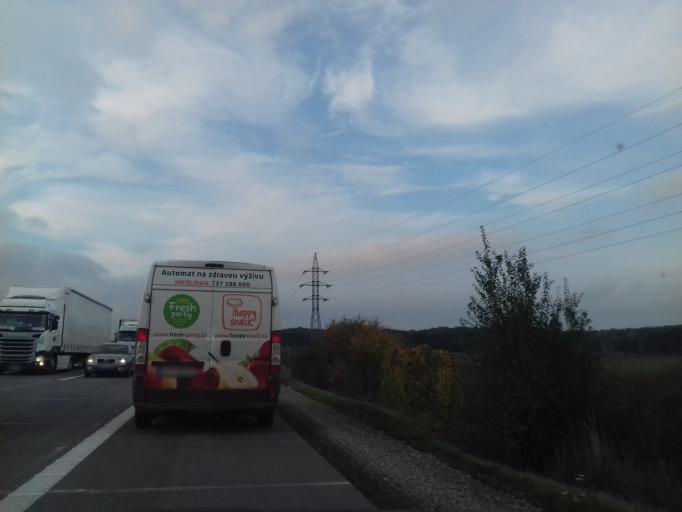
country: CZ
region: South Moravian
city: Nosislav
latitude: 49.0272
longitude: 16.6849
